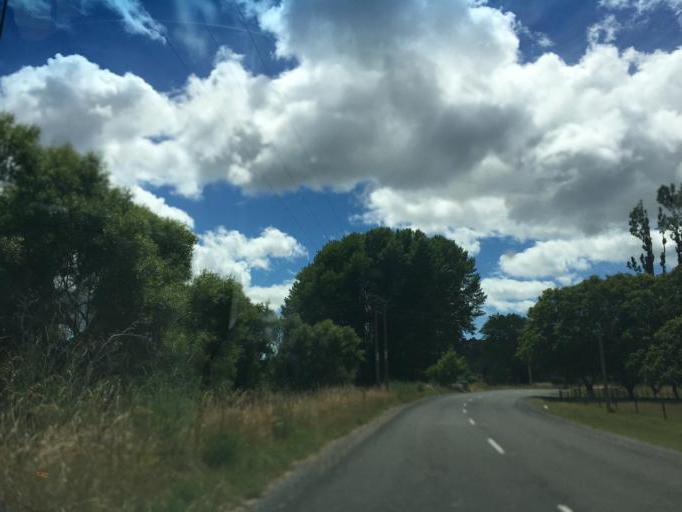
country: NZ
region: Hawke's Bay
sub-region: Hastings District
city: Hastings
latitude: -39.7482
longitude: 176.8808
